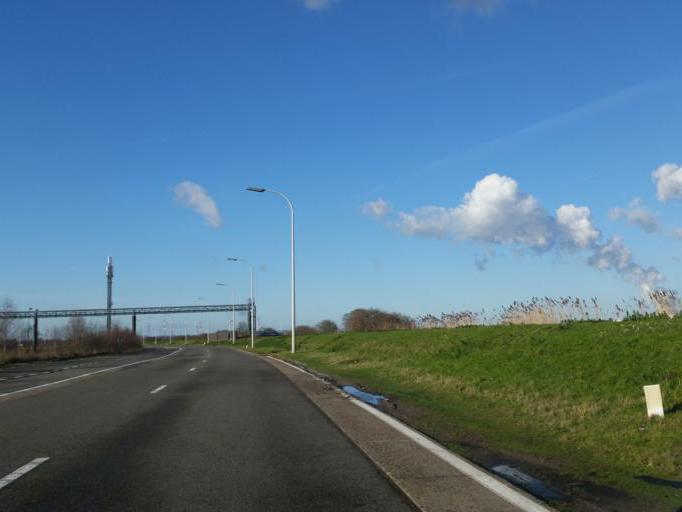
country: BE
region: Flanders
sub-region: Provincie Antwerpen
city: Zwijndrecht
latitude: 51.2476
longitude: 4.3273
